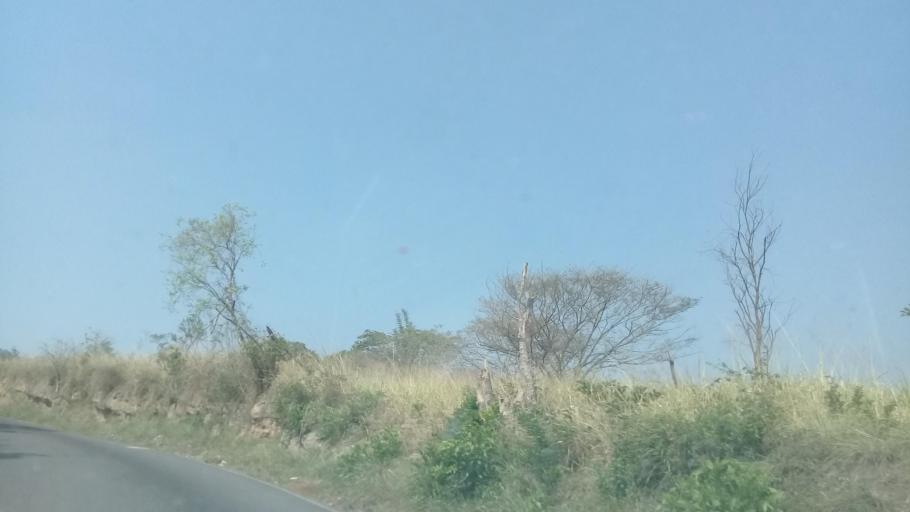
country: MX
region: Veracruz
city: El Castillo
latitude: 19.5771
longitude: -96.8314
